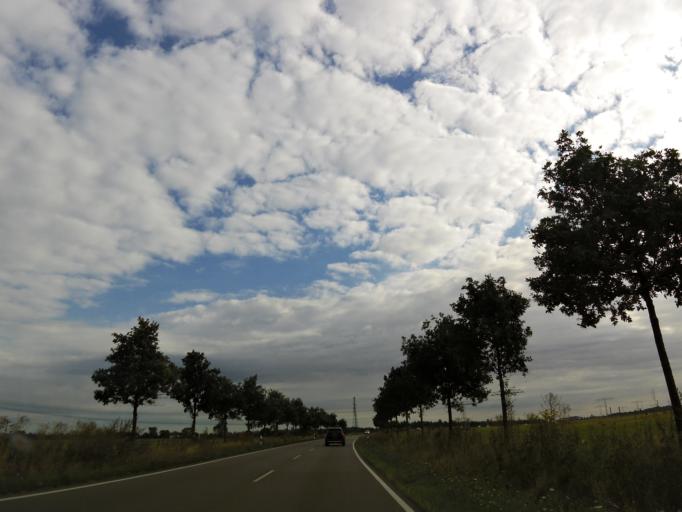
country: DE
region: Saxony
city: Markranstadt
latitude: 51.2869
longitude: 12.2860
